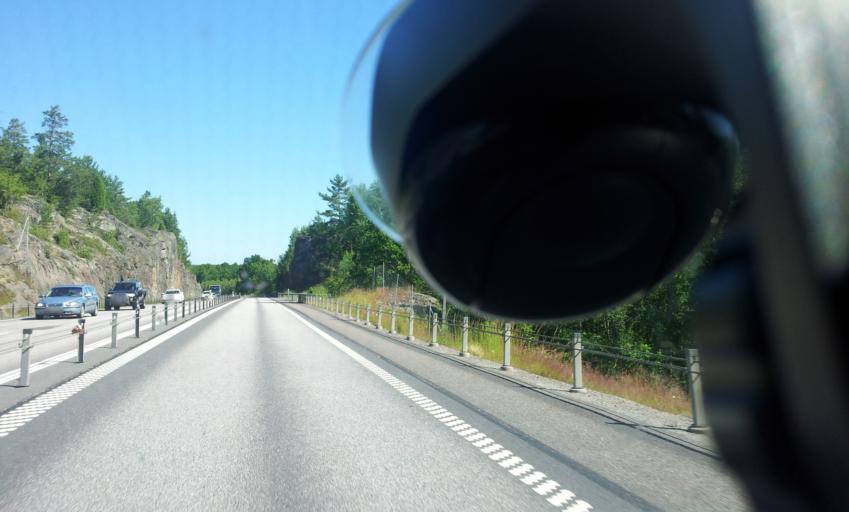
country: SE
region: OEstergoetland
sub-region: Valdemarsviks Kommun
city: Gusum
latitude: 58.3493
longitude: 16.4471
